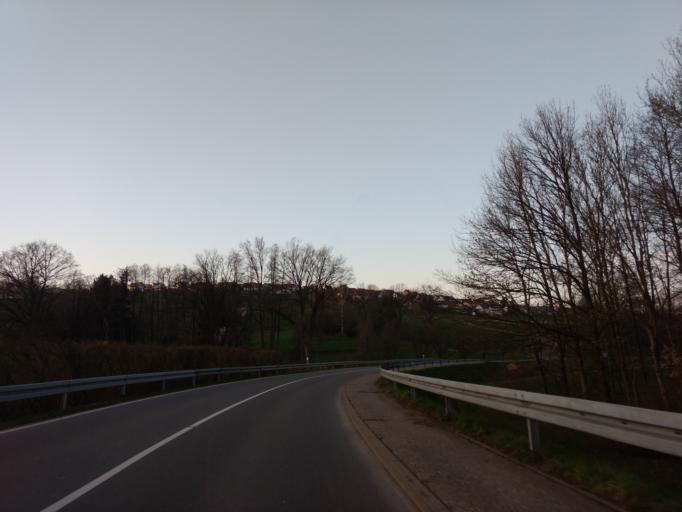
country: DE
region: Baden-Wuerttemberg
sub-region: Regierungsbezirk Stuttgart
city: Lorch
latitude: 48.7943
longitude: 9.6511
